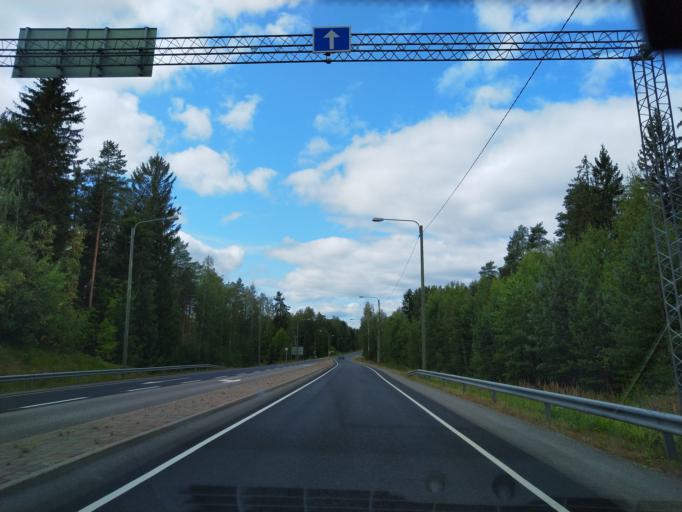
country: FI
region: Haeme
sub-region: Riihimaeki
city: Loppi
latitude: 60.7220
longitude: 24.4411
